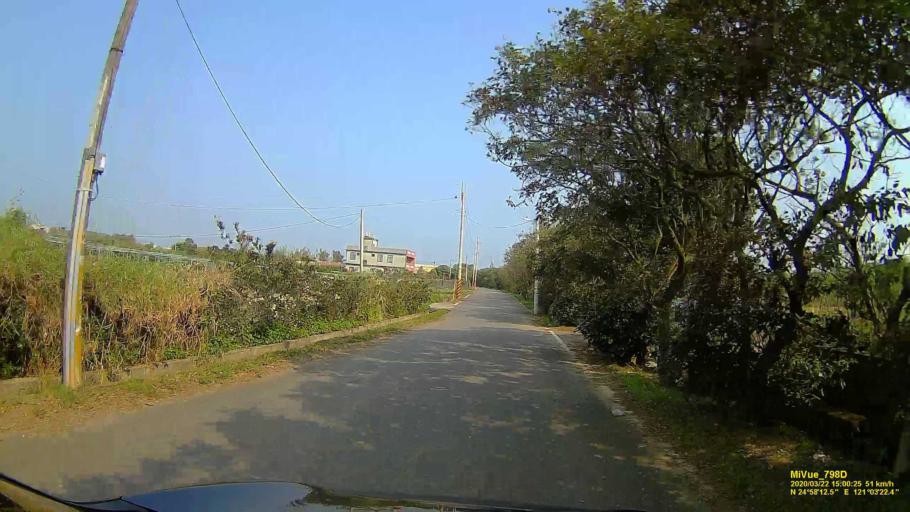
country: TW
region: Taiwan
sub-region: Hsinchu
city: Zhubei
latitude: 24.9700
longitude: 121.0565
